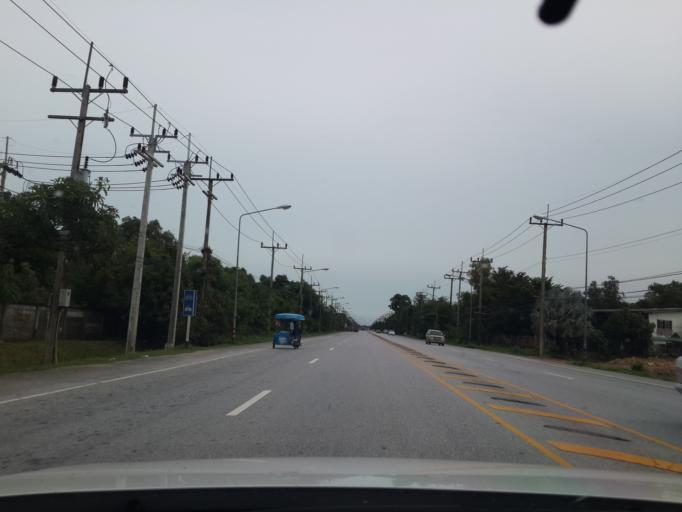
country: TH
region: Pattani
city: Nong Chik
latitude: 6.8154
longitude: 101.1583
